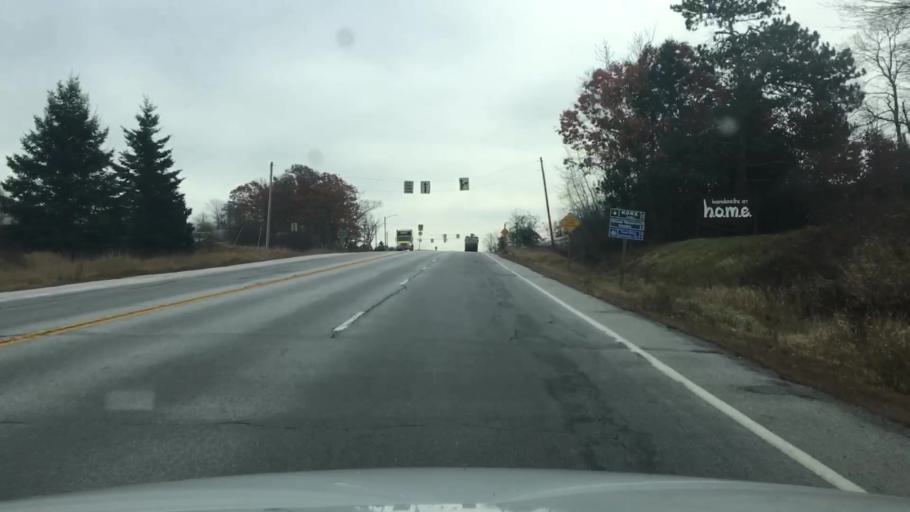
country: US
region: Maine
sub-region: Hancock County
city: Orland
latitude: 44.5752
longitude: -68.7338
